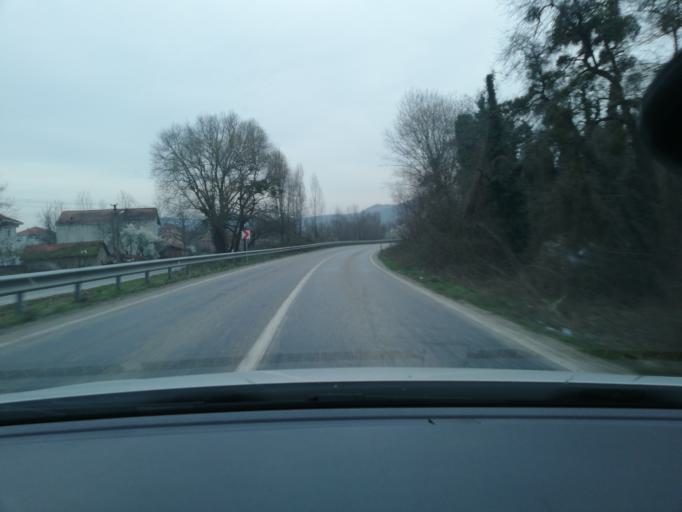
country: TR
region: Zonguldak
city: Saltukova
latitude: 41.5221
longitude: 32.0911
